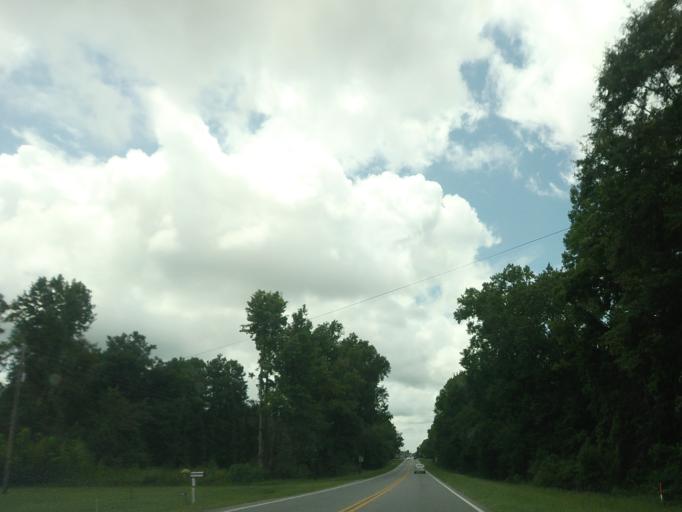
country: US
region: Georgia
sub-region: Bleckley County
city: Cochran
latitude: 32.3999
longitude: -83.3391
